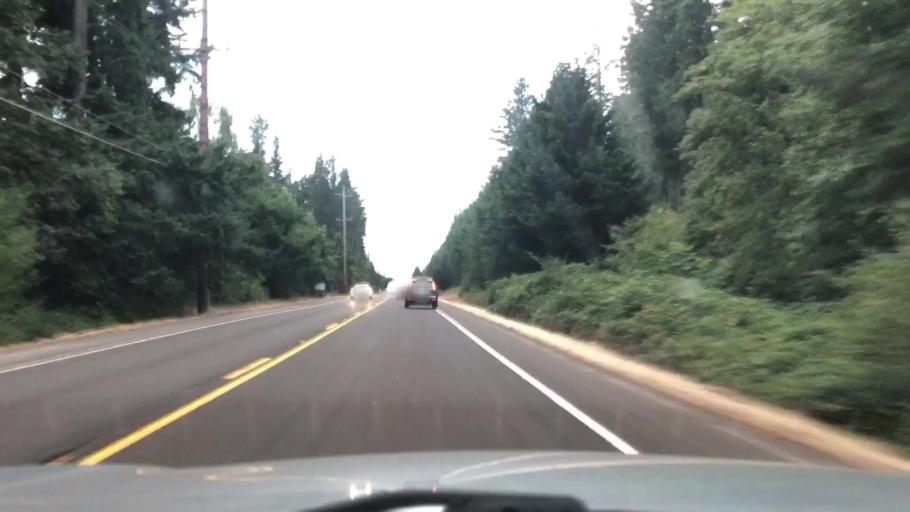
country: US
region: Oregon
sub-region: Clackamas County
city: Beavercreek
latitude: 45.2830
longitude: -122.5666
